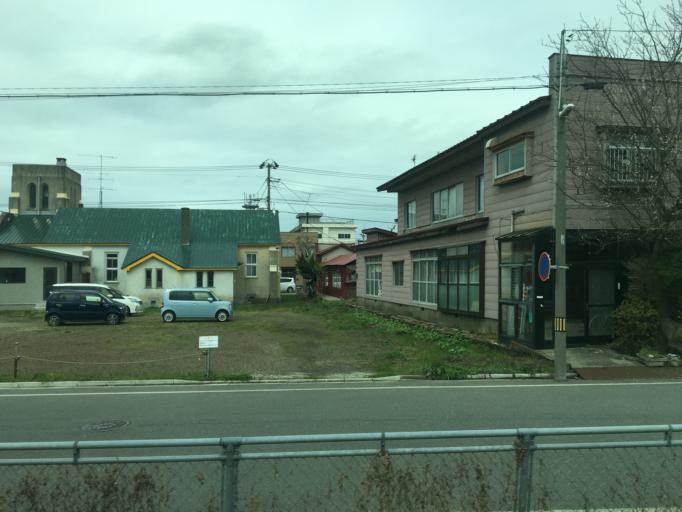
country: JP
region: Akita
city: Noshiromachi
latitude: 40.2106
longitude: 140.0337
